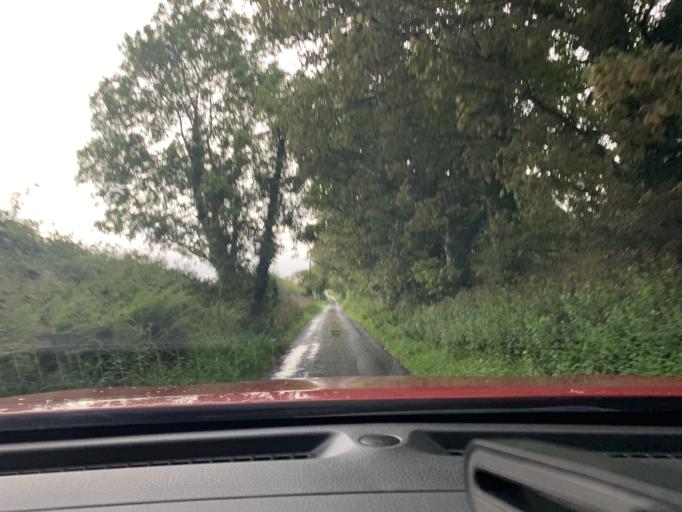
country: IE
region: Connaught
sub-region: Sligo
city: Strandhill
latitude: 54.3578
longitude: -8.5504
